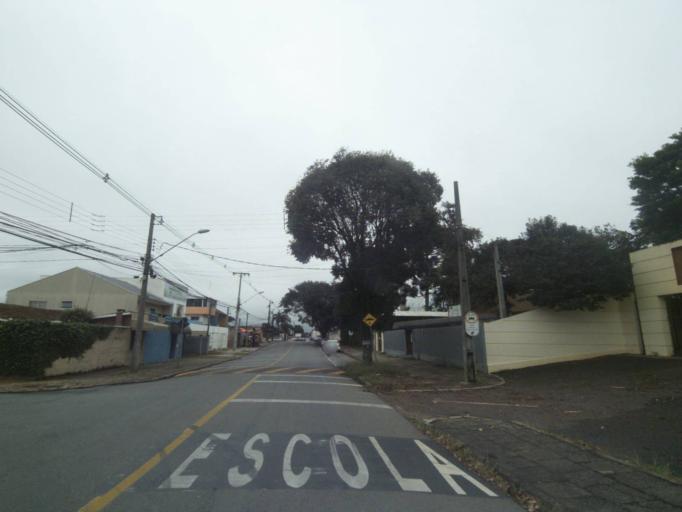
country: BR
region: Parana
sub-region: Curitiba
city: Curitiba
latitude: -25.5015
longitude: -49.3009
